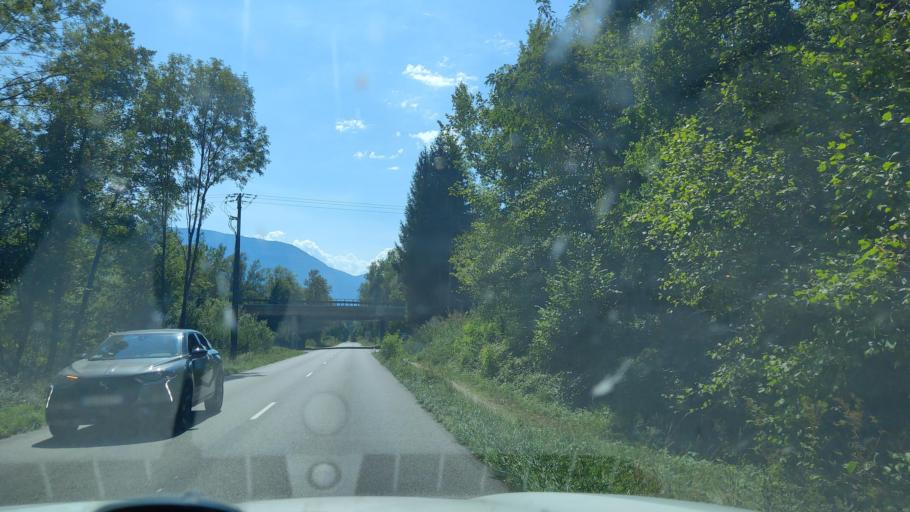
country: FR
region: Rhone-Alpes
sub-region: Departement de la Savoie
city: Novalaise
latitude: 45.5781
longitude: 5.7934
